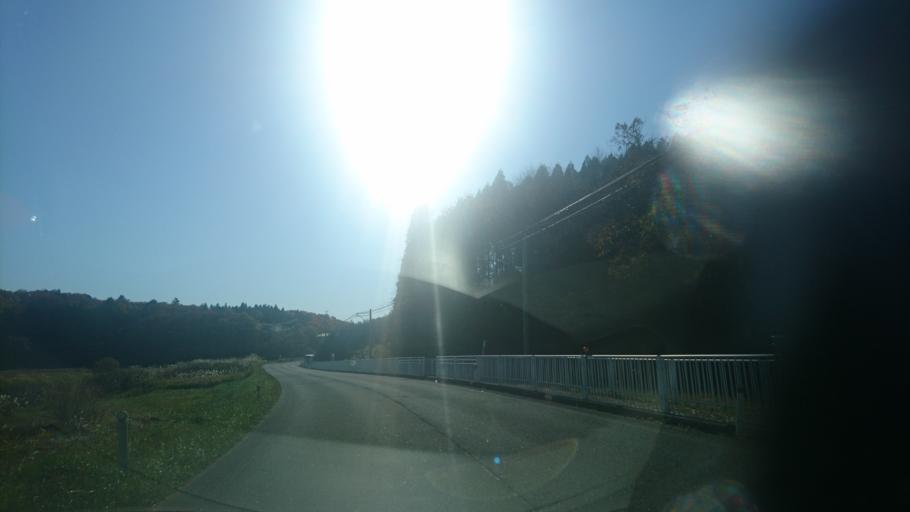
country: JP
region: Miyagi
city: Tomiya
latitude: 38.4016
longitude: 140.8665
